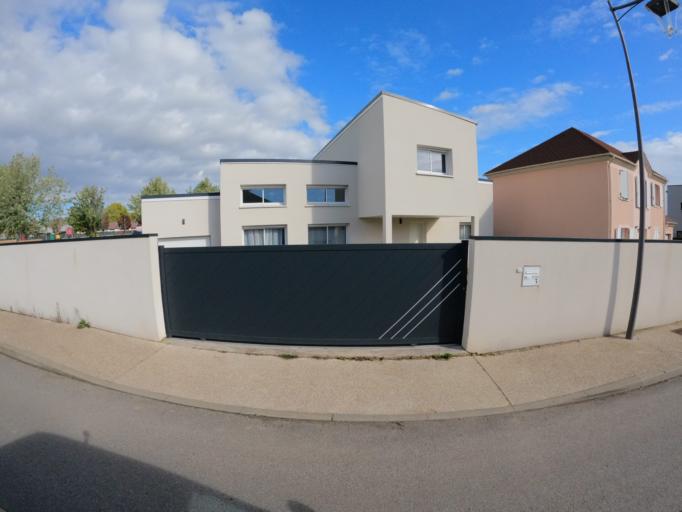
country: FR
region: Ile-de-France
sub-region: Departement de Seine-et-Marne
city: Montry
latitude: 48.8830
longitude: 2.8330
